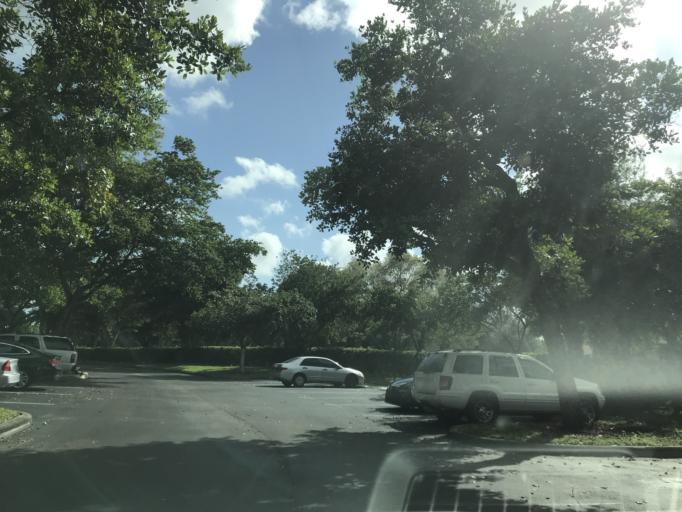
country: US
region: Florida
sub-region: Broward County
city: Coconut Creek
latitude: 26.2694
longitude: -80.1880
